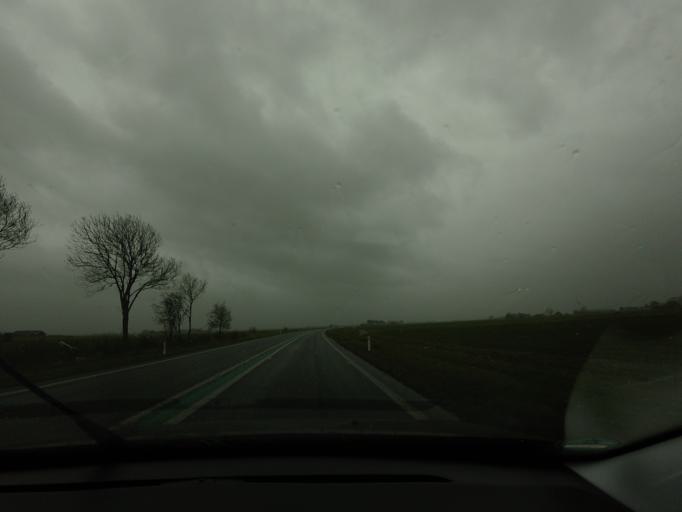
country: NL
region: Friesland
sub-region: Gemeente Littenseradiel
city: Wommels
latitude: 53.1049
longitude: 5.5774
